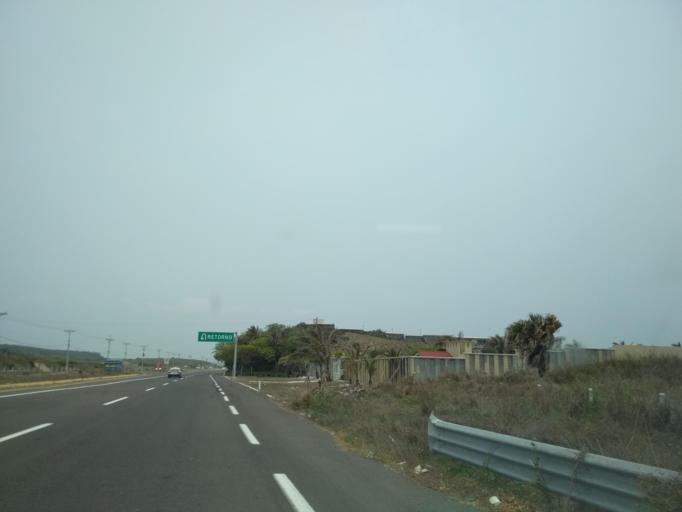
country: MX
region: Veracruz
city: Anton Lizardo
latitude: 19.0531
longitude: -96.0268
